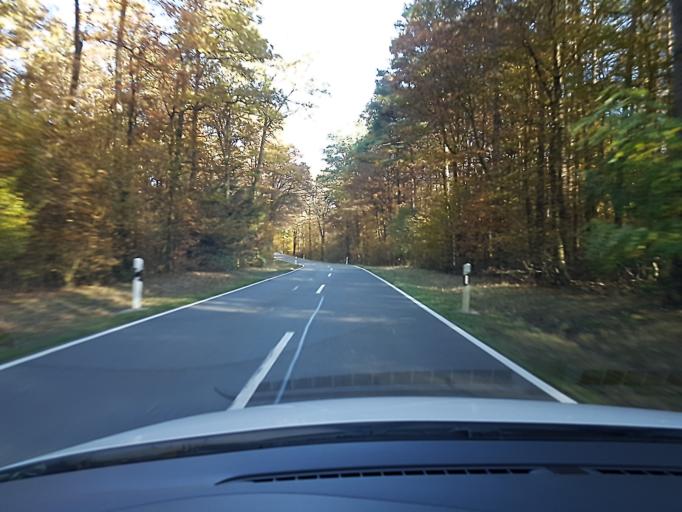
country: DE
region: Baden-Wuerttemberg
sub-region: Karlsruhe Region
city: Fahrenbach
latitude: 49.4034
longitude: 9.1858
